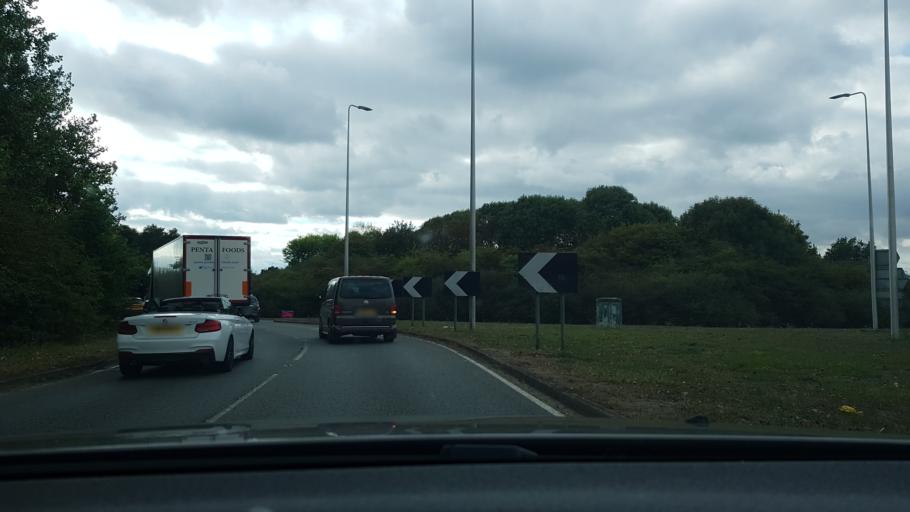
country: GB
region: England
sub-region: West Berkshire
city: Theale
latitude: 51.4316
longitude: -1.0897
